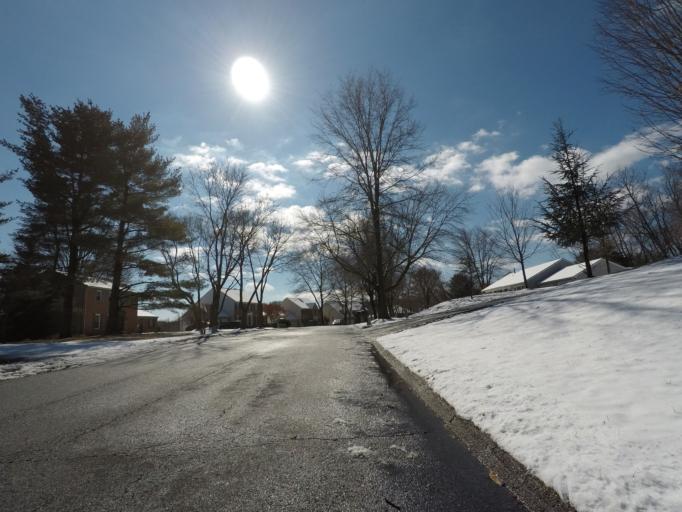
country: US
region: Maryland
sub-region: Howard County
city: Columbia
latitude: 39.2696
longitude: -76.8543
